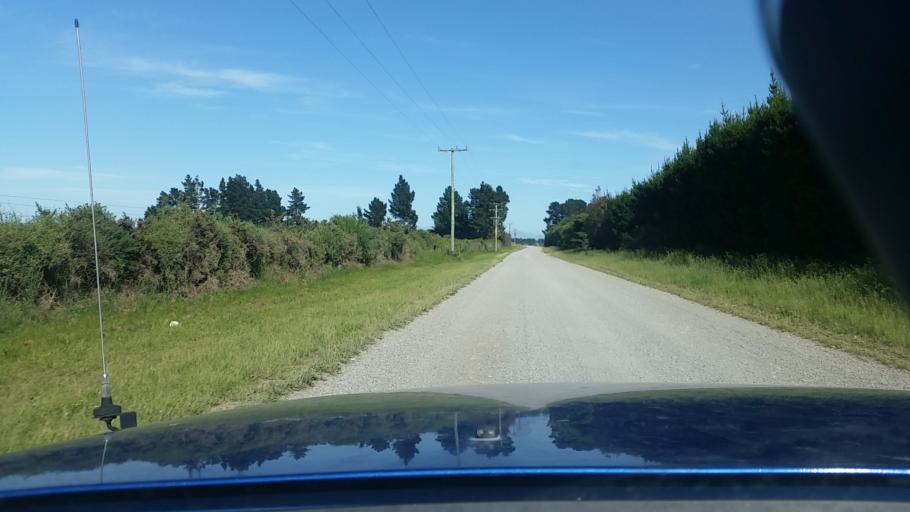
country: NZ
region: Canterbury
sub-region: Ashburton District
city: Ashburton
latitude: -43.9574
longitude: 171.8827
